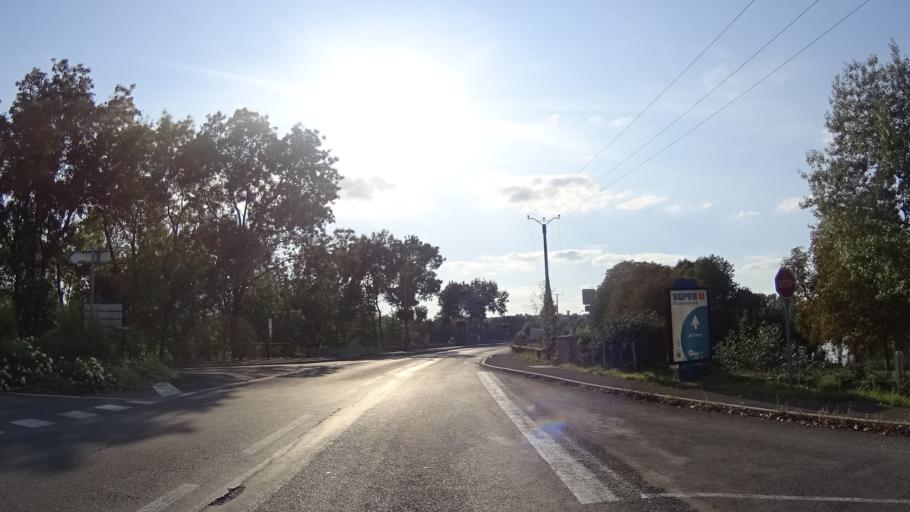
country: FR
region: Pays de la Loire
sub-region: Departement de Maine-et-Loire
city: Chalonnes-sur-Loire
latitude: 47.3501
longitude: -0.7495
